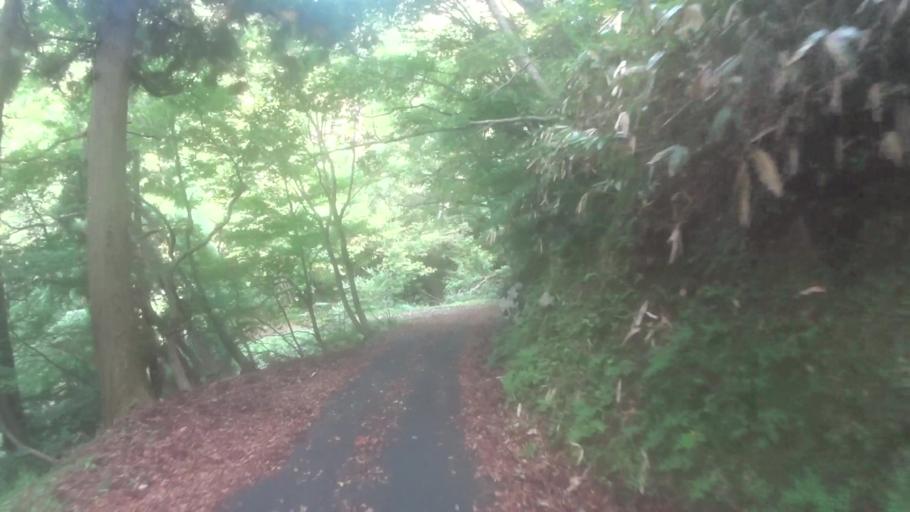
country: JP
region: Kyoto
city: Miyazu
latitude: 35.6249
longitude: 135.1598
